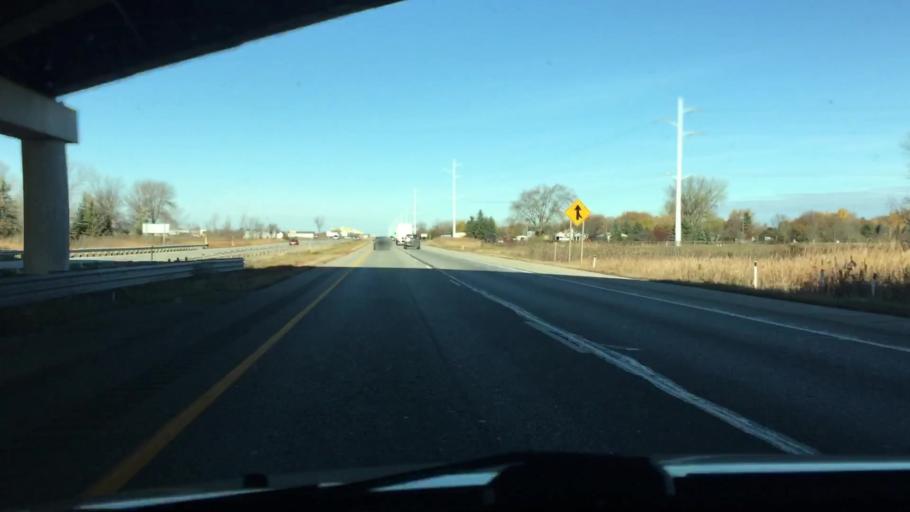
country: US
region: Wisconsin
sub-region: Fond du Lac County
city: North Fond du Lac
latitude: 43.8067
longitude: -88.4998
